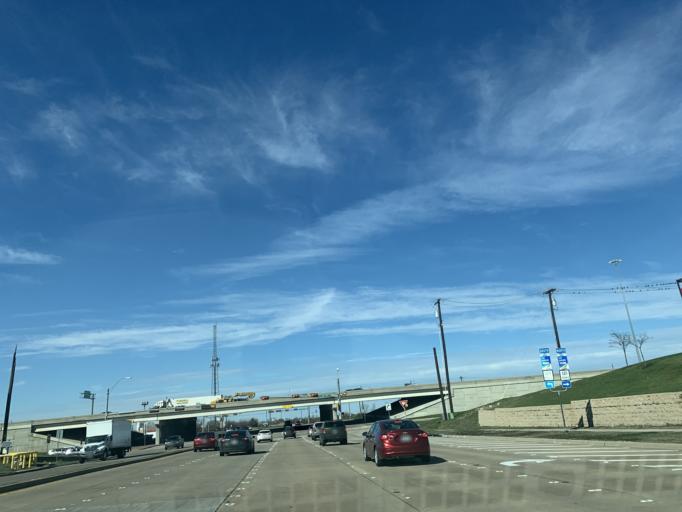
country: US
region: Texas
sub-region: Denton County
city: The Colony
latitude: 33.0814
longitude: -96.8513
